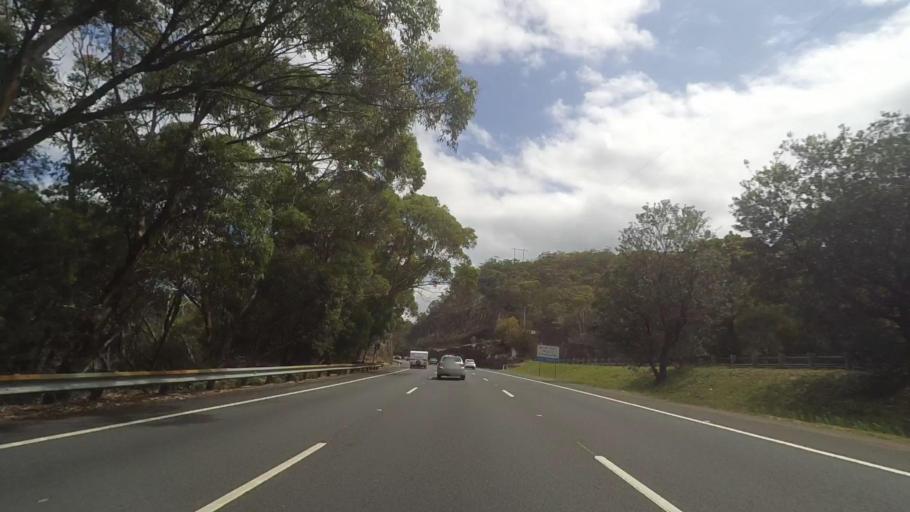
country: AU
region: New South Wales
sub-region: Hornsby Shire
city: Berowra
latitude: -33.5515
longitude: 151.1932
